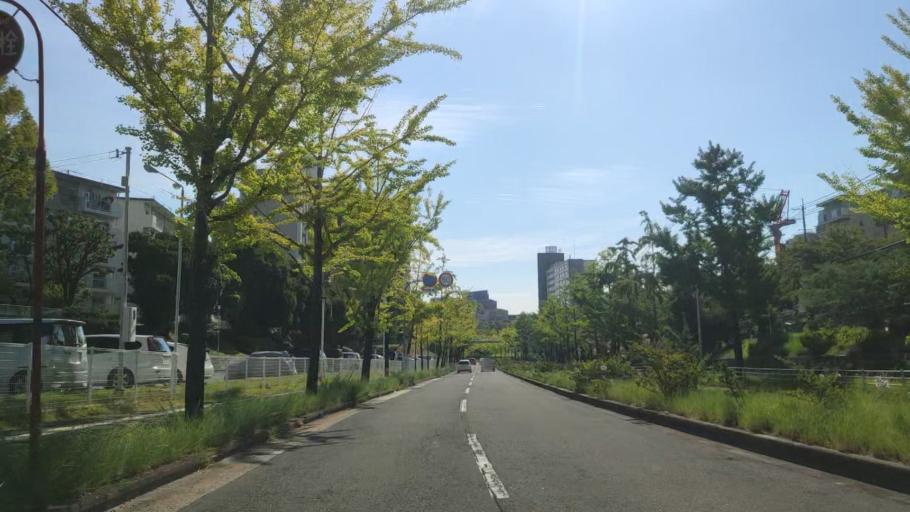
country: JP
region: Osaka
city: Suita
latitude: 34.7938
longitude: 135.5041
